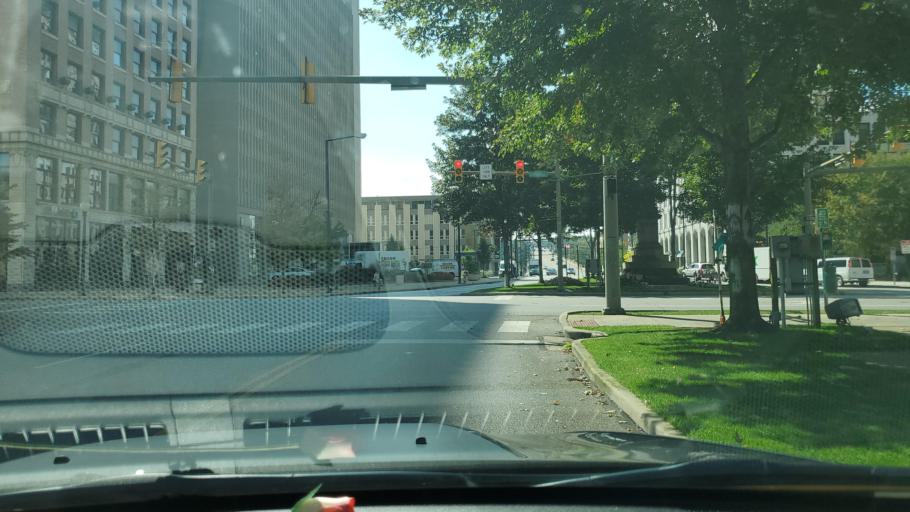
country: US
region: Ohio
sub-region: Mahoning County
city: Youngstown
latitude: 41.1002
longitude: -80.6491
